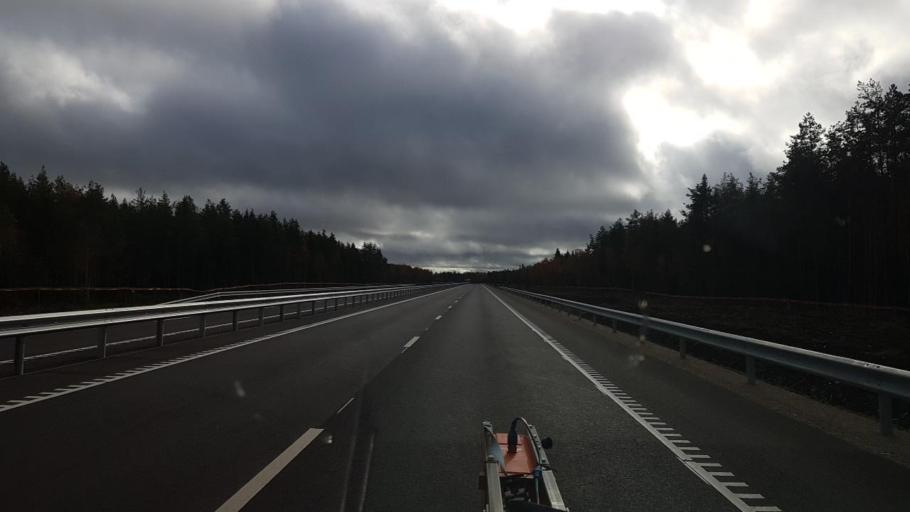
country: EE
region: Jaervamaa
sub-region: Paide linn
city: Paide
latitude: 59.0193
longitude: 25.5493
